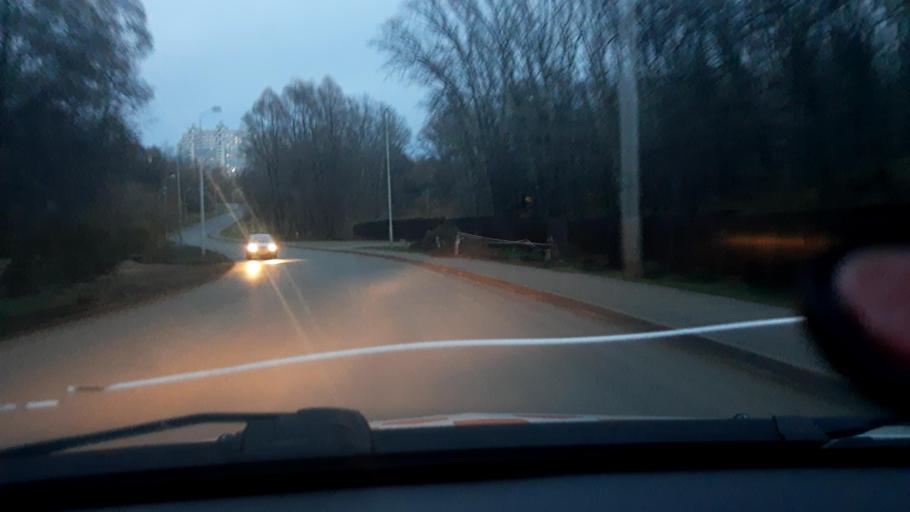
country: RU
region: Bashkortostan
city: Ufa
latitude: 54.8124
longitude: 56.0464
